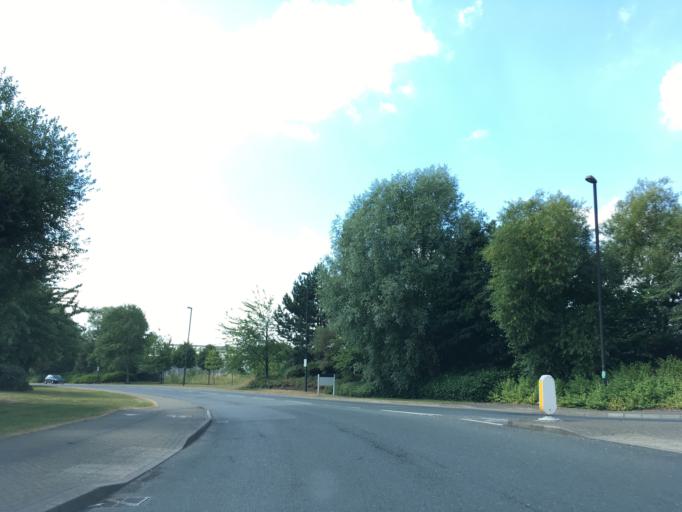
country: GB
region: England
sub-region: Gloucestershire
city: Churchdown
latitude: 51.8462
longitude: -2.1722
